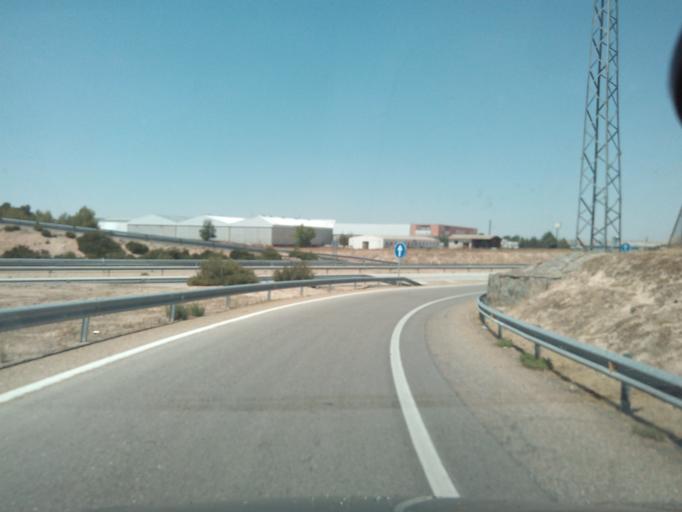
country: ES
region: Castille-La Mancha
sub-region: Province of Toledo
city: Tembleque
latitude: 39.6882
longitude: -3.4993
